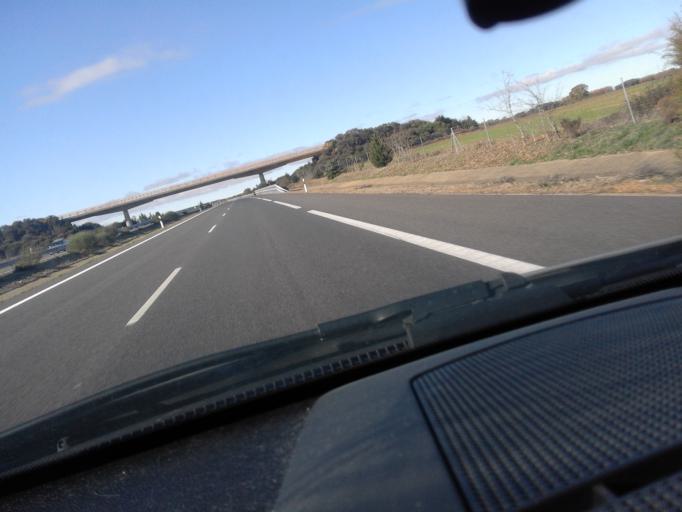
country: ES
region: Castille and Leon
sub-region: Provincia de Palencia
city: Bustillo del Paramo de Carrion
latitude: 42.3584
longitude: -4.7928
